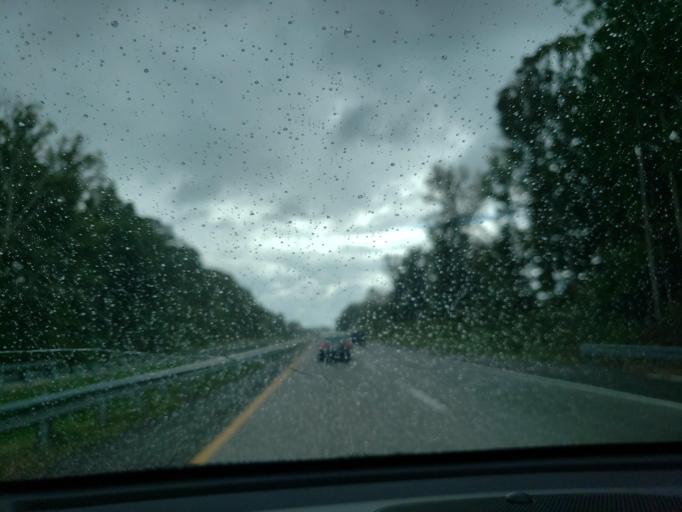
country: US
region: North Carolina
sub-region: Warren County
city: Norlina
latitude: 36.5046
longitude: -78.2134
